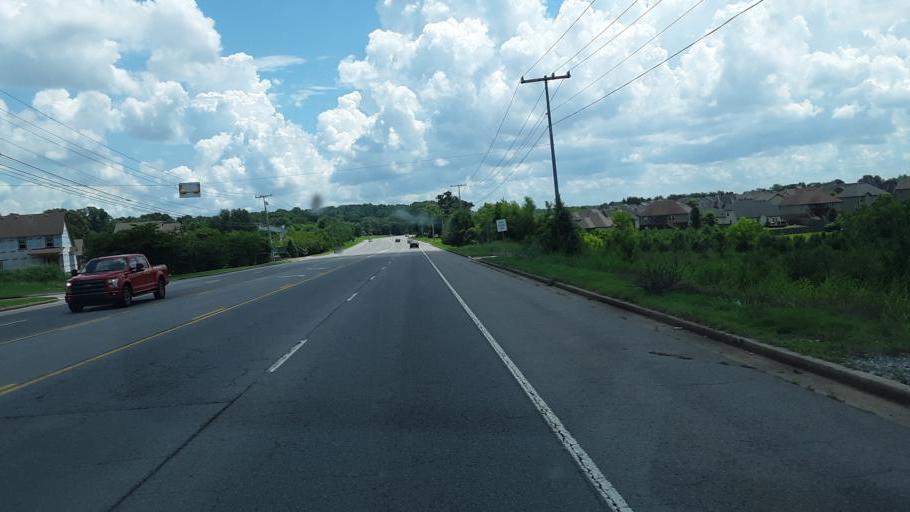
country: US
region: Kentucky
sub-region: Christian County
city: Oak Grove
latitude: 36.6307
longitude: -87.3809
